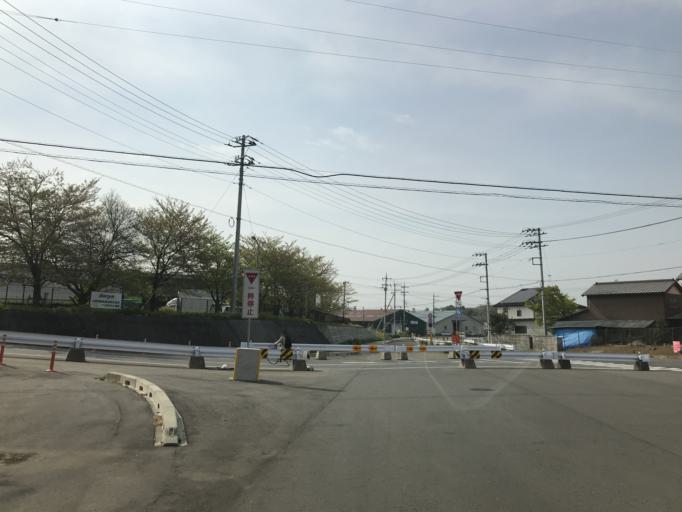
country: JP
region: Ibaraki
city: Moriya
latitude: 35.9694
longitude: 139.9901
